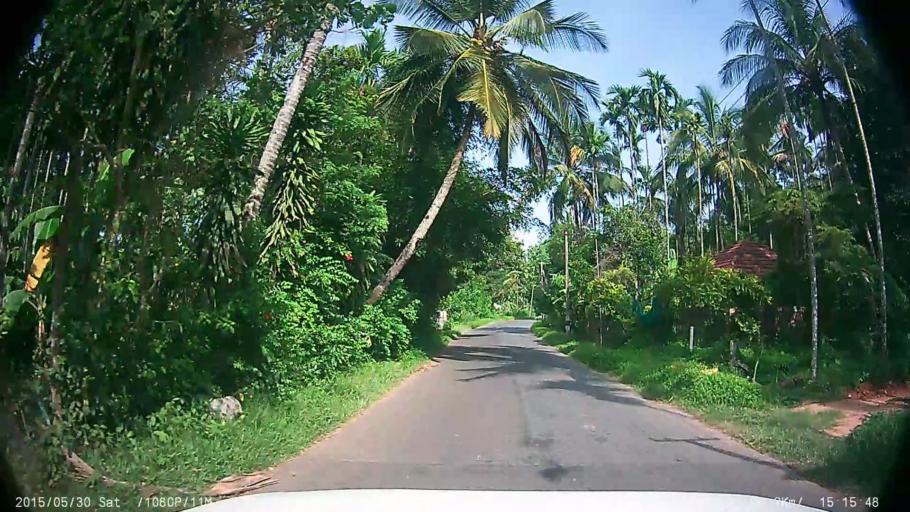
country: IN
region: Kerala
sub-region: Wayanad
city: Panamaram
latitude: 11.7781
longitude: 76.0510
